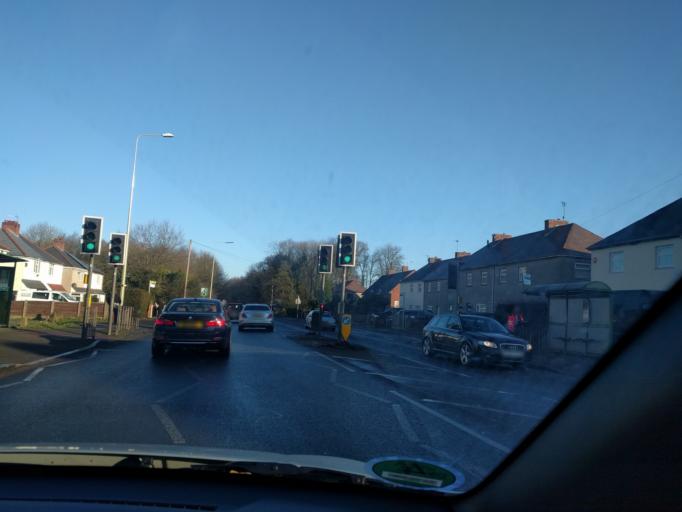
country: GB
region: England
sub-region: Staffordshire
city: Featherstone
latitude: 52.6474
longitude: -2.0835
